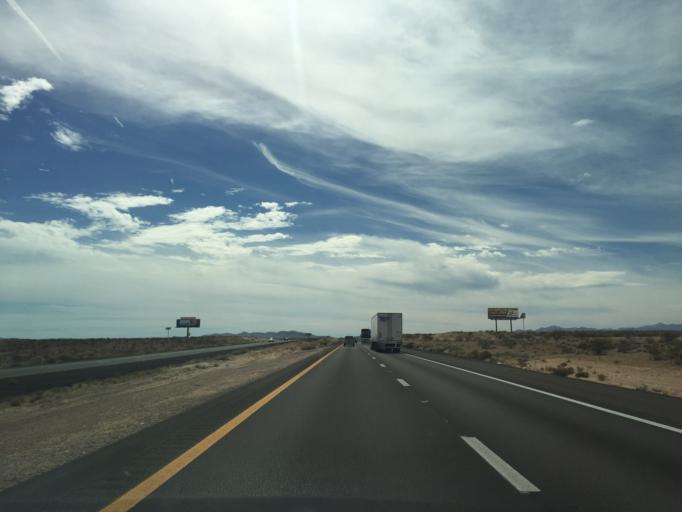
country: US
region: Nevada
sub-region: Clark County
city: Moapa Town
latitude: 36.5255
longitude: -114.7310
